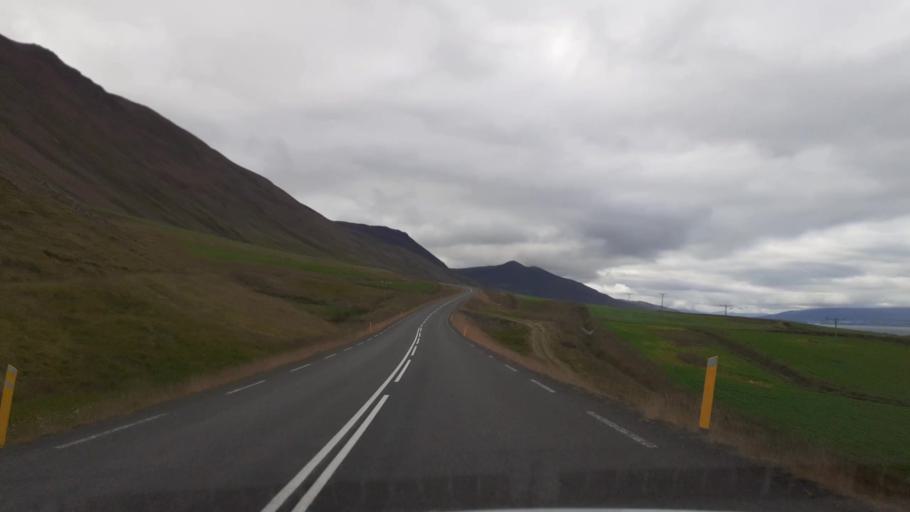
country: IS
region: Northeast
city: Akureyri
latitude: 65.8668
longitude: -18.0750
